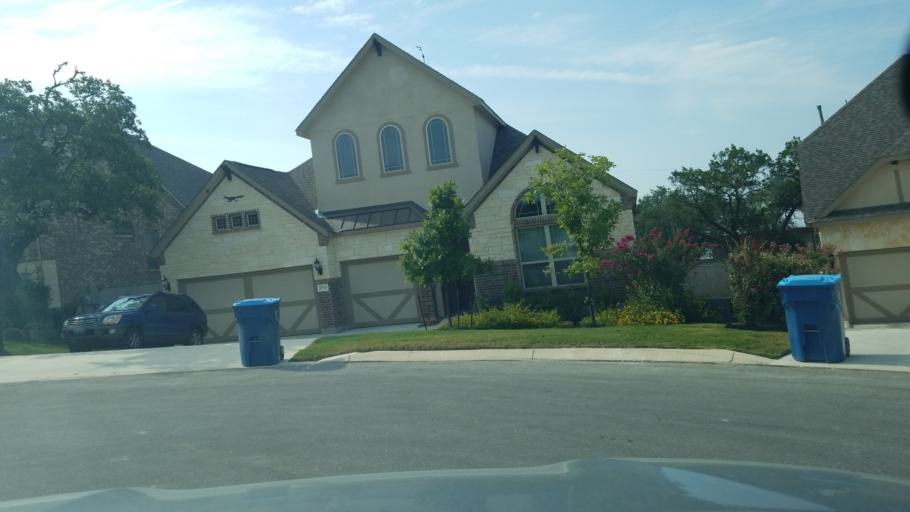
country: US
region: Texas
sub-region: Bexar County
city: Scenic Oaks
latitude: 29.7243
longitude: -98.6599
